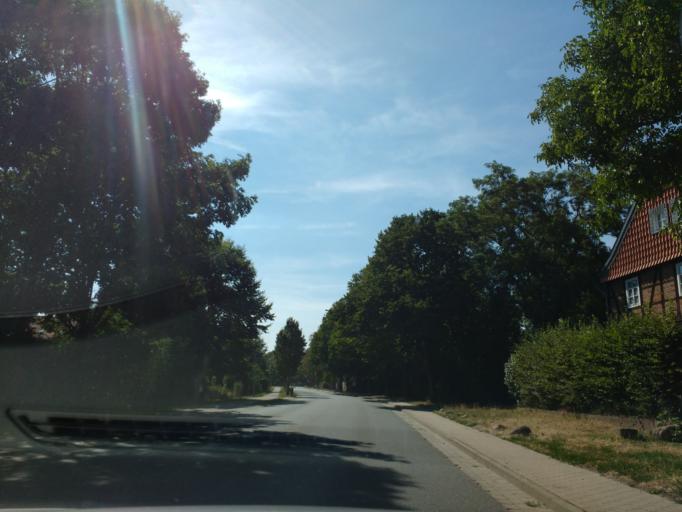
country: DE
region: Lower Saxony
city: Schellerten
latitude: 52.1802
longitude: 10.0688
